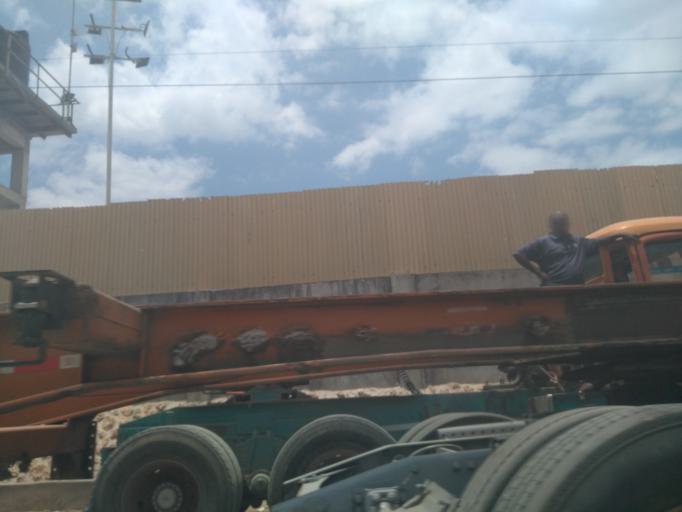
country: TZ
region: Dar es Salaam
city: Dar es Salaam
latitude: -6.8631
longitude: 39.2812
